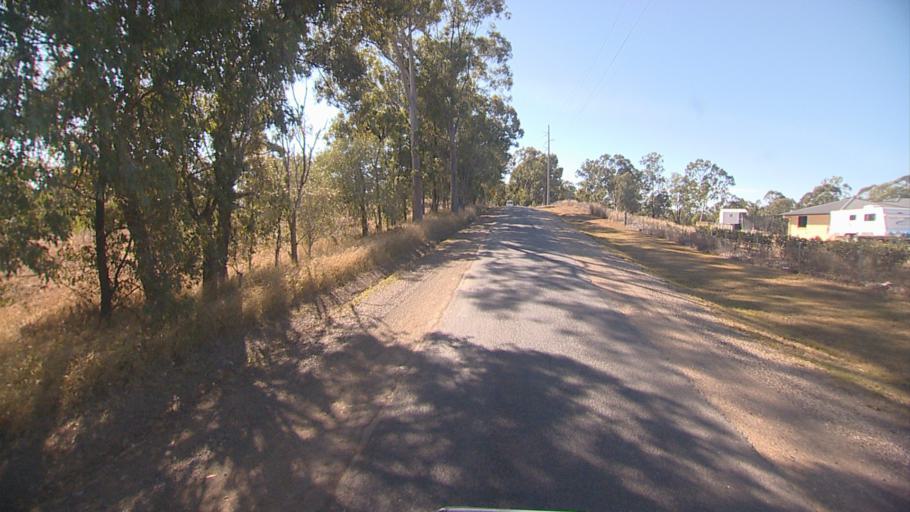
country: AU
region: Queensland
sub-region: Logan
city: Cedar Vale
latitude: -27.8939
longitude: 153.0166
